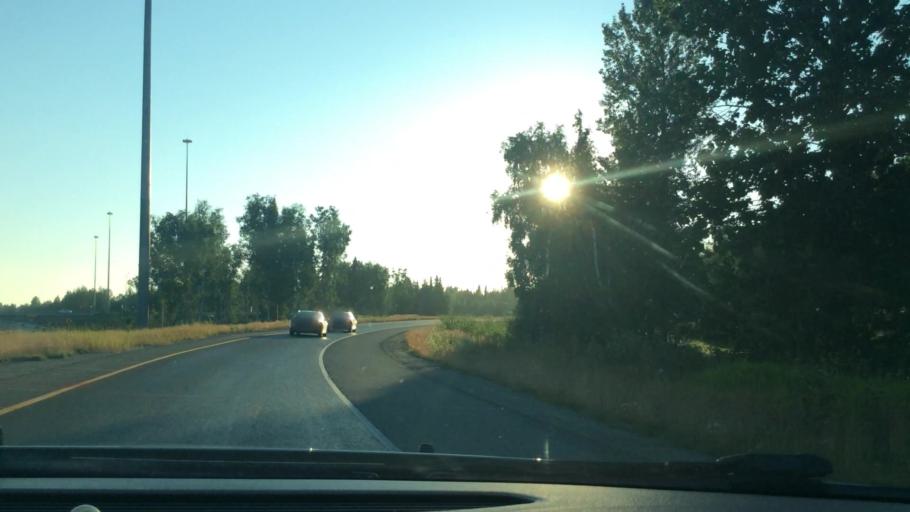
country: US
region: Alaska
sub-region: Anchorage Municipality
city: Anchorage
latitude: 61.2249
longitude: -149.7720
